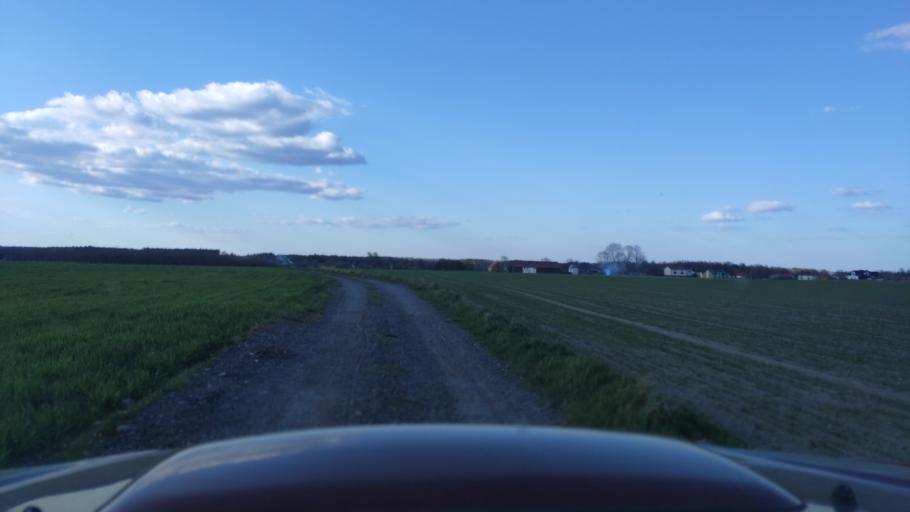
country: PL
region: Masovian Voivodeship
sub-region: Powiat zwolenski
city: Zwolen
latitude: 51.3761
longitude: 21.5757
